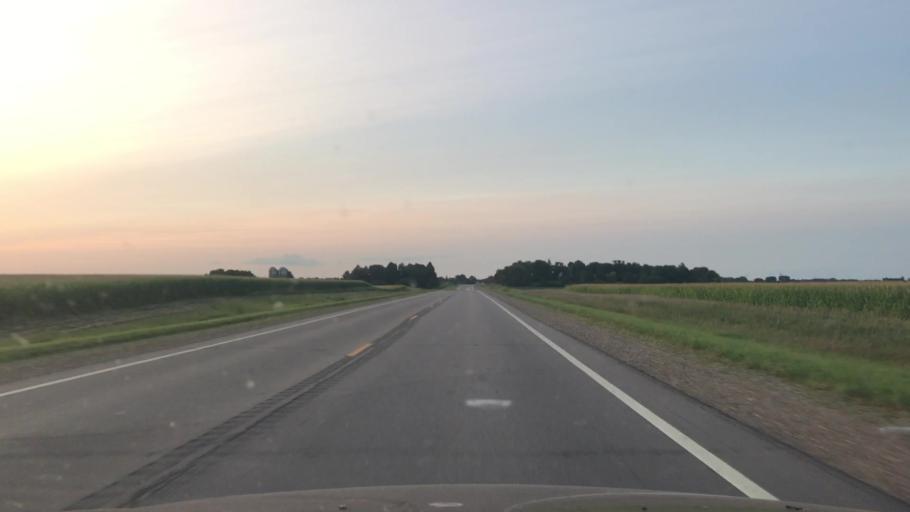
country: US
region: Minnesota
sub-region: Redwood County
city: Redwood Falls
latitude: 44.5123
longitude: -95.1180
